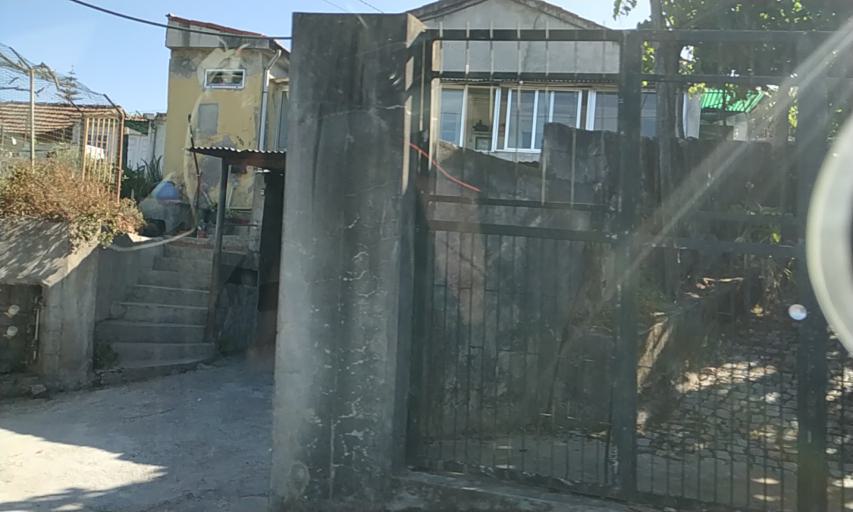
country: PT
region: Porto
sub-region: Santo Tirso
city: Santo Tirso
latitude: 41.3411
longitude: -8.4885
